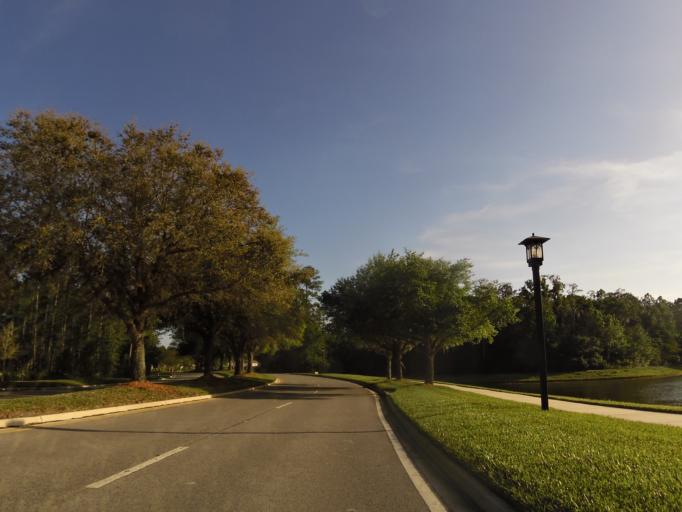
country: US
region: Florida
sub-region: Saint Johns County
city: Villano Beach
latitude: 29.9781
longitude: -81.4763
